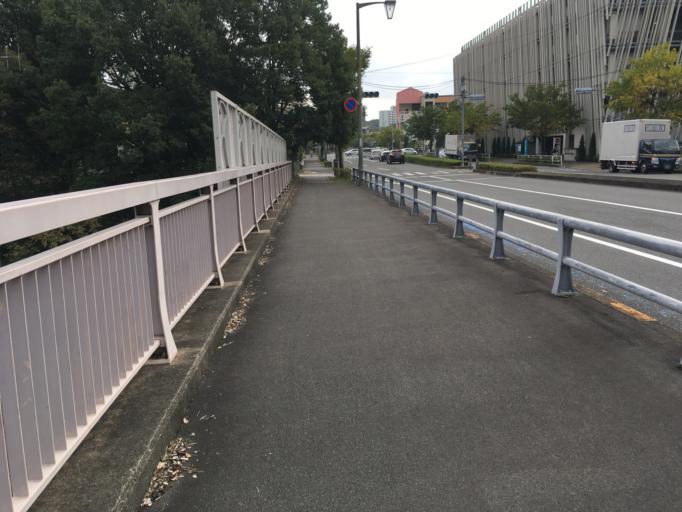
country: JP
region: Tokyo
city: Hino
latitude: 35.6149
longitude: 139.3812
